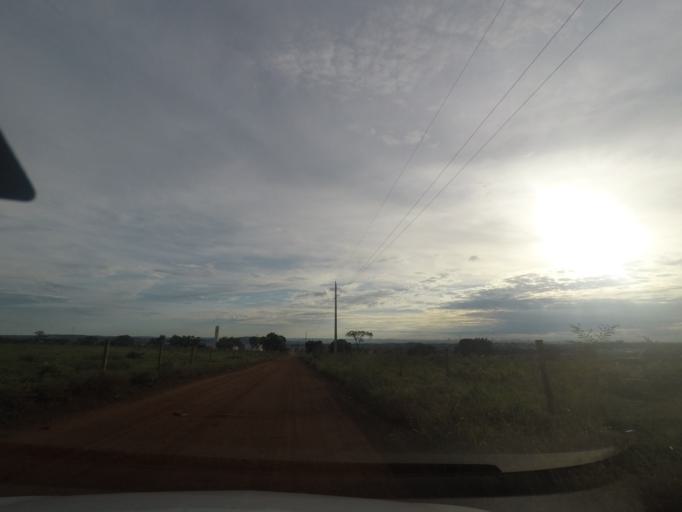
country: BR
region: Goias
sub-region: Trindade
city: Trindade
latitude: -16.7316
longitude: -49.4131
